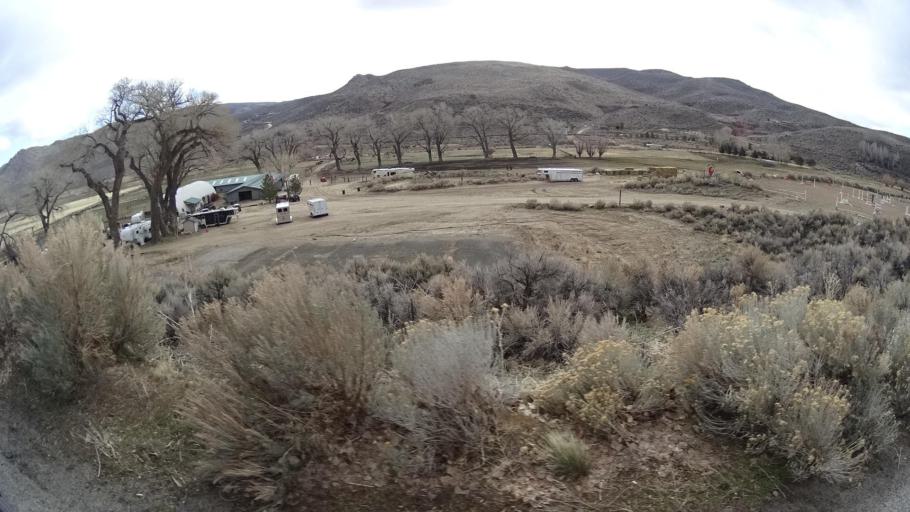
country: US
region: Nevada
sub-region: Washoe County
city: Cold Springs
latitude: 39.8386
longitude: -119.9356
